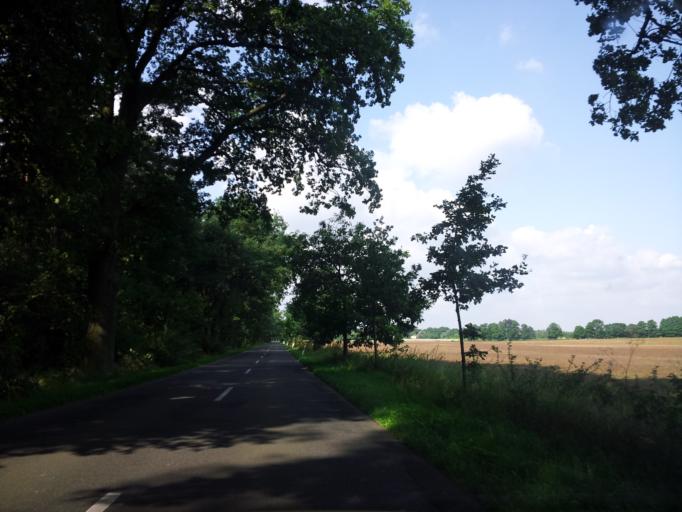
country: DE
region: Brandenburg
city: Treuenbrietzen
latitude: 52.0782
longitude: 12.8948
